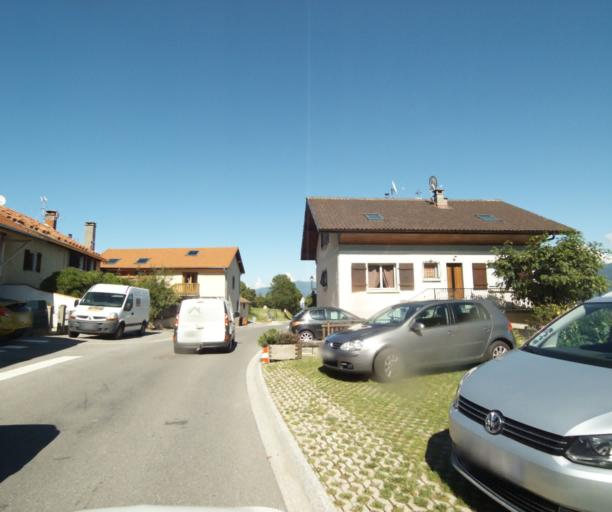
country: FR
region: Rhone-Alpes
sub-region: Departement de la Haute-Savoie
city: Ballaison
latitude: 46.2962
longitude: 6.3541
